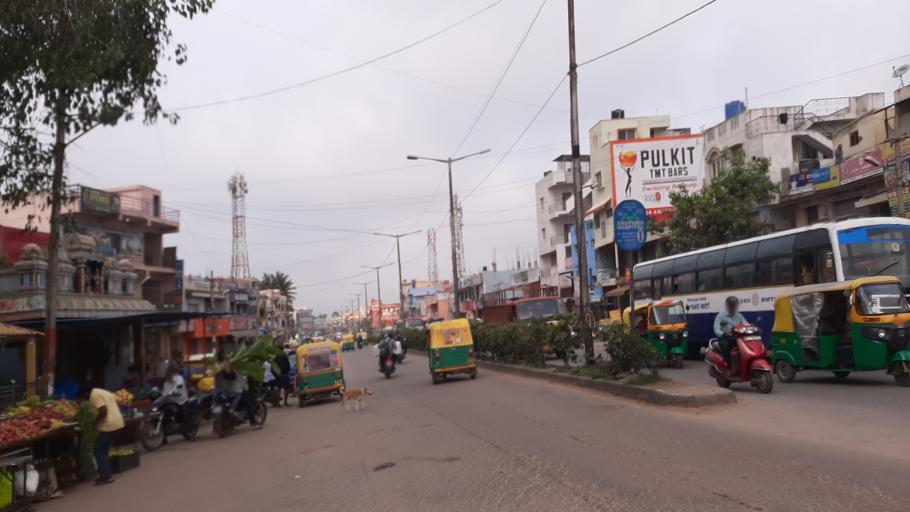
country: IN
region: Karnataka
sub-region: Bangalore Urban
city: Bangalore
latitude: 12.9861
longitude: 77.4883
